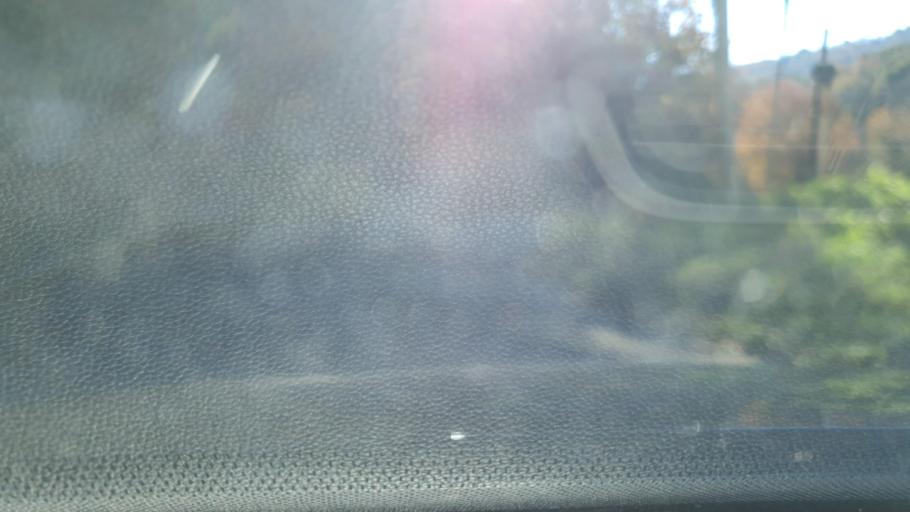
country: IT
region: Calabria
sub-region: Provincia di Catanzaro
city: Sant'Elia
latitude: 38.9643
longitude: 16.5792
